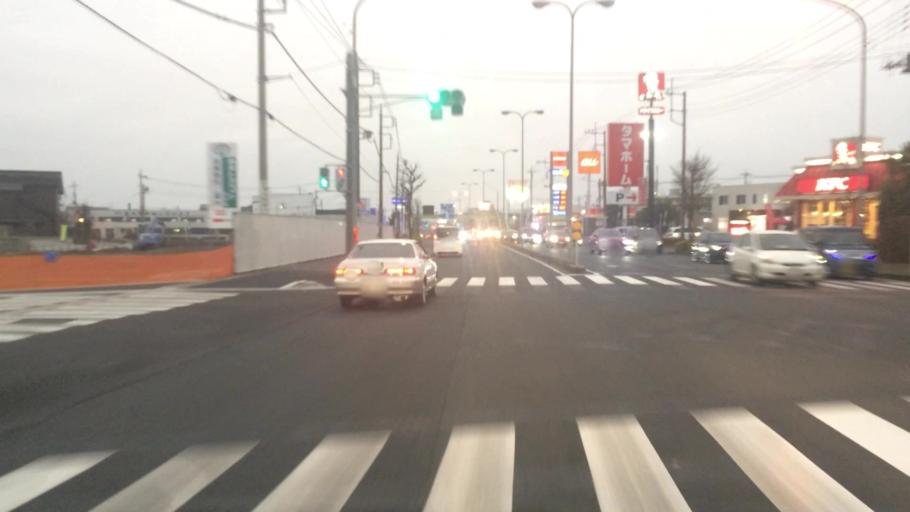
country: JP
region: Tochigi
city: Utsunomiya-shi
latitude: 36.5839
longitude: 139.8503
